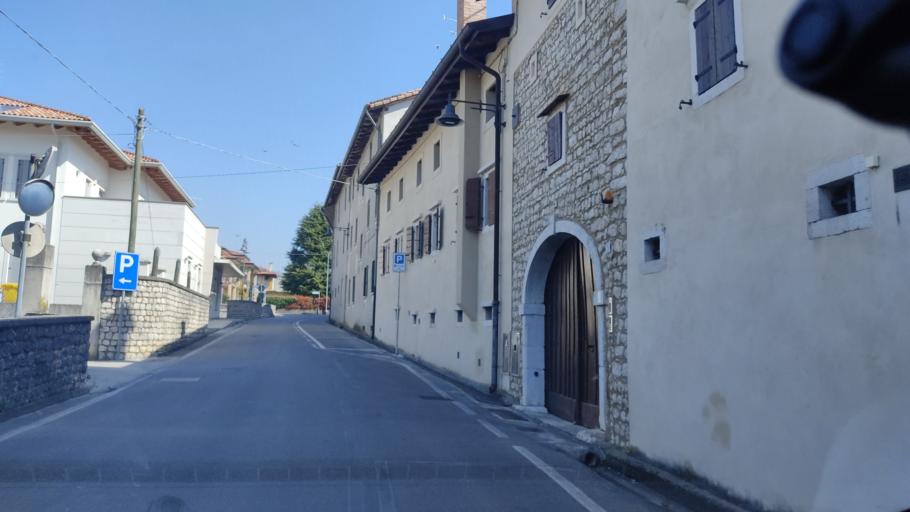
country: IT
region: Friuli Venezia Giulia
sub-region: Provincia di Pordenone
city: Budoia
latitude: 46.0445
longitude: 12.5306
